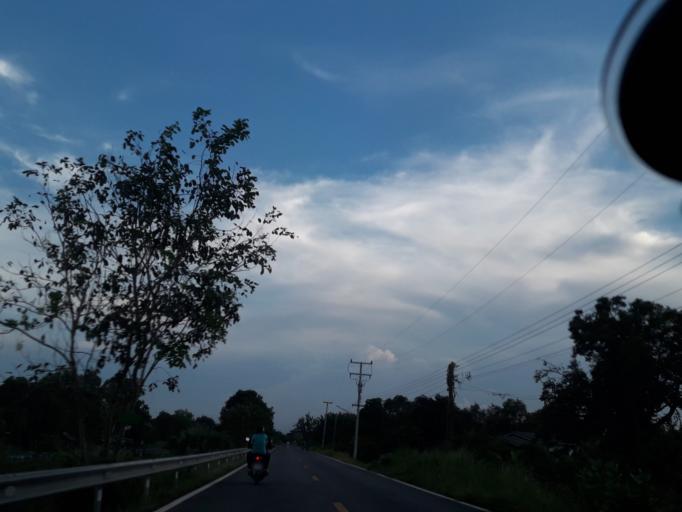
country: TH
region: Sara Buri
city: Nong Khae
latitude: 14.2824
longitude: 100.8912
